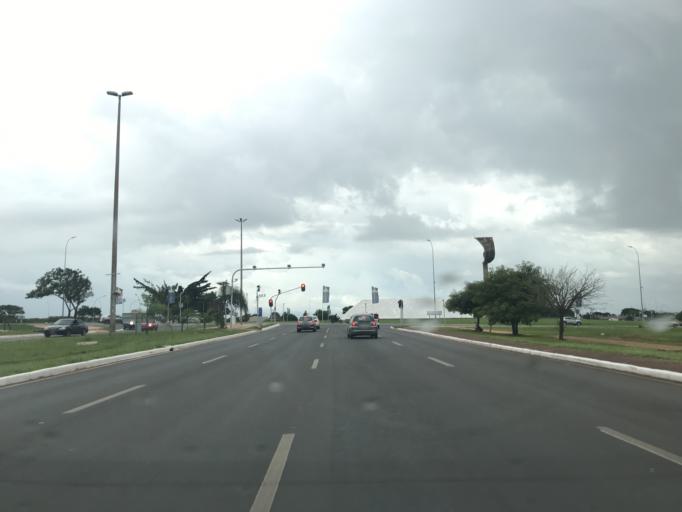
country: BR
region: Federal District
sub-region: Brasilia
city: Brasilia
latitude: -15.7859
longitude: -47.9141
